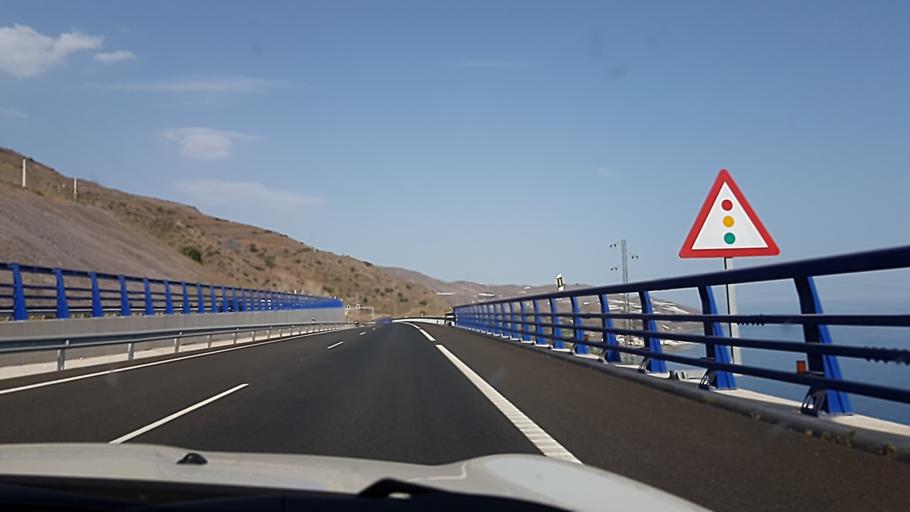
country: ES
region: Andalusia
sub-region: Provincia de Granada
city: Sorvilan
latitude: 36.7549
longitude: -3.2632
